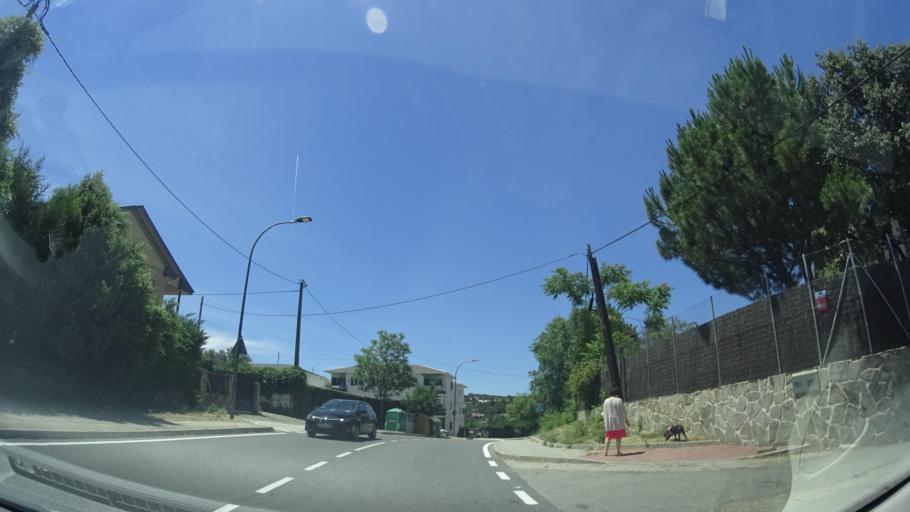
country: ES
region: Madrid
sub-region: Provincia de Madrid
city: Galapagar
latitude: 40.6027
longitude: -3.9835
